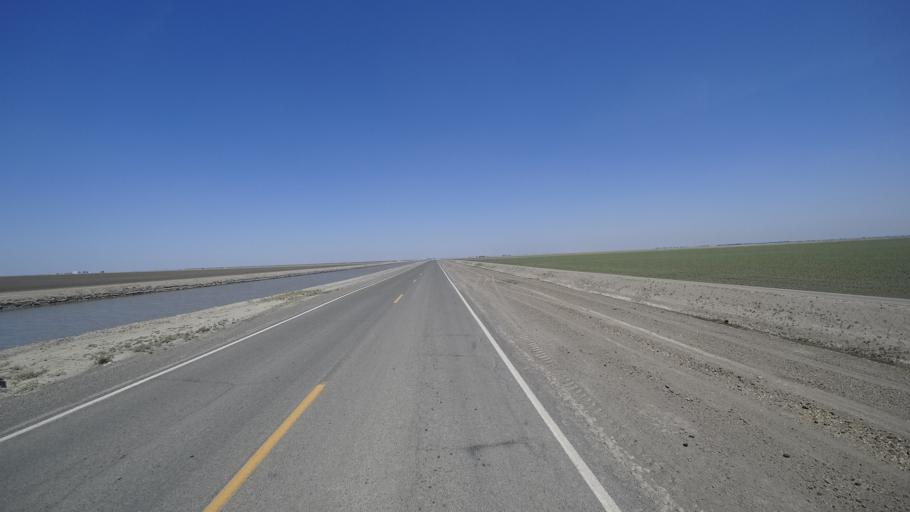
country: US
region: California
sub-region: Kings County
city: Corcoran
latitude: 36.0534
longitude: -119.6437
